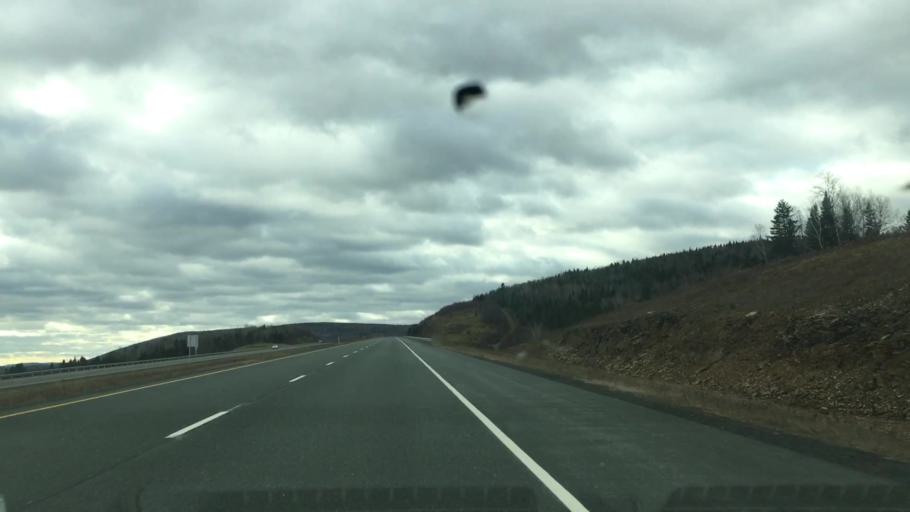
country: US
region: Maine
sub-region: Aroostook County
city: Fort Fairfield
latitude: 46.7218
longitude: -67.7306
